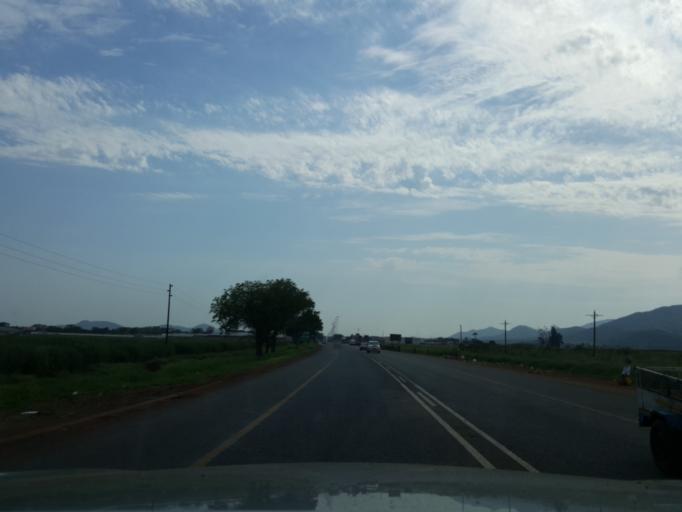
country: SZ
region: Hhohho
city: Ntfonjeni
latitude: -25.5039
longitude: 31.4995
